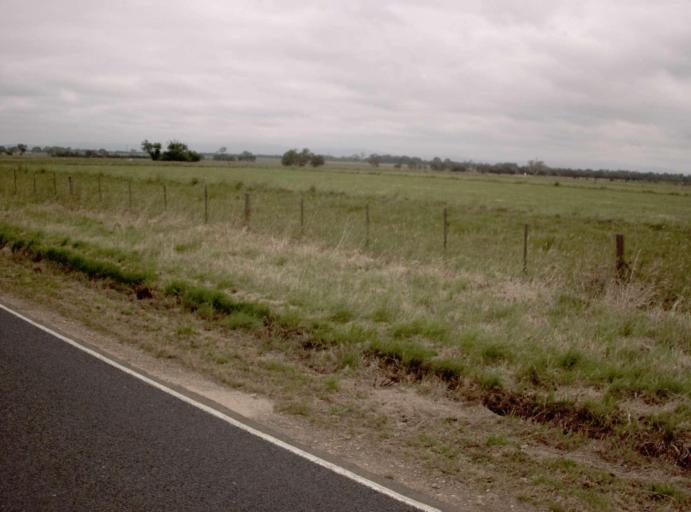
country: AU
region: Victoria
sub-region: Wellington
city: Heyfield
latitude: -38.0351
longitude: 146.9246
